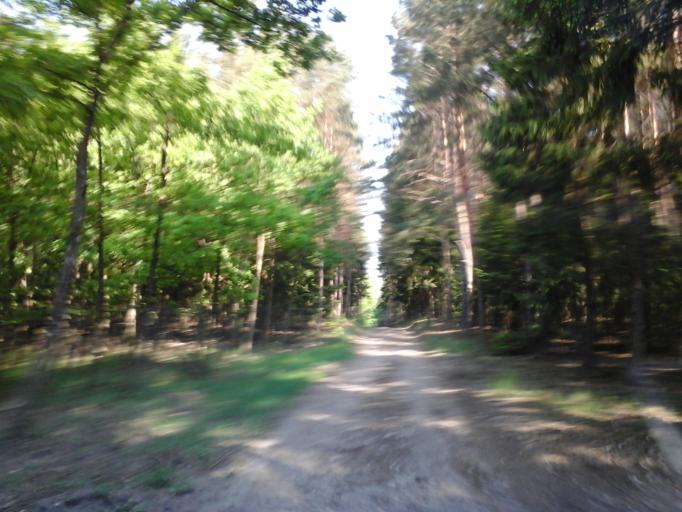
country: PL
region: West Pomeranian Voivodeship
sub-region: Powiat choszczenski
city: Recz
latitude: 53.3303
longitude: 15.5255
